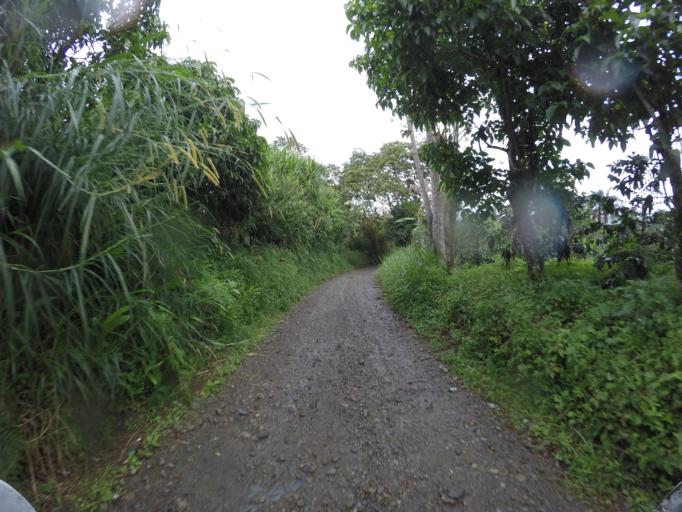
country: CO
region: Valle del Cauca
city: Ulloa
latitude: 4.6825
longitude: -75.7082
